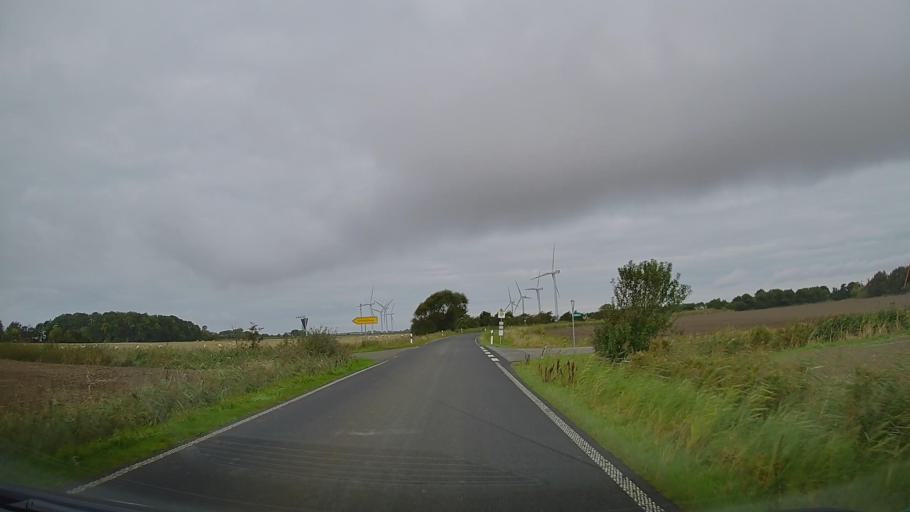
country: DE
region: Schleswig-Holstein
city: Galmsbull
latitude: 54.7679
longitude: 8.7166
